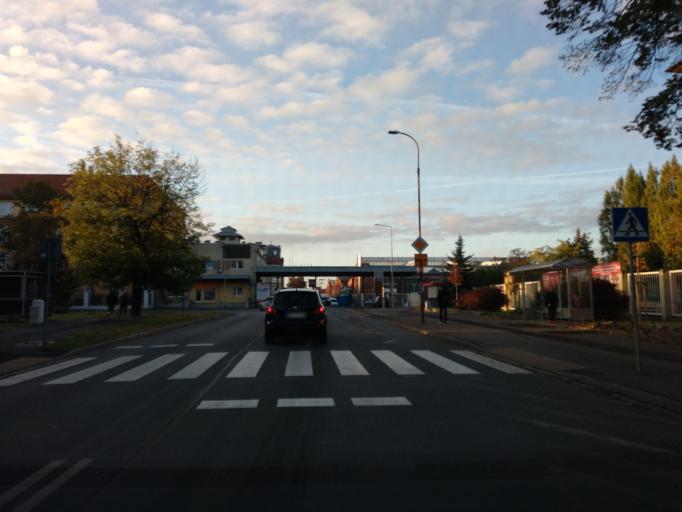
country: PL
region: Lower Silesian Voivodeship
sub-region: Powiat wroclawski
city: Wroclaw
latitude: 51.1129
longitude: 16.9888
